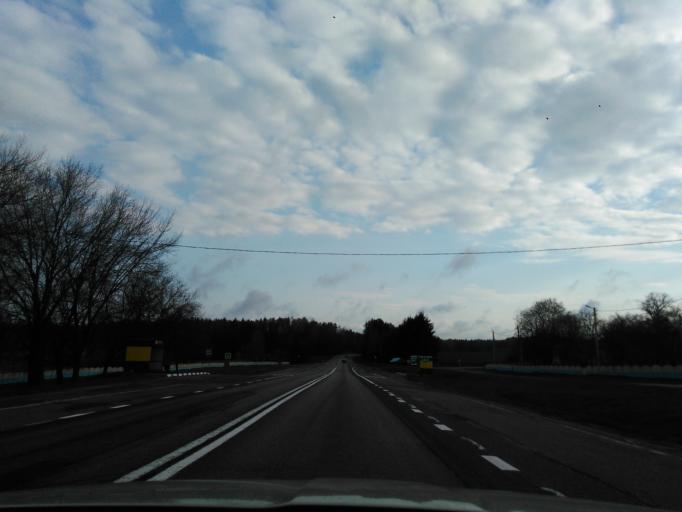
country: BY
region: Minsk
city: Lahoysk
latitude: 54.2911
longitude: 27.8722
